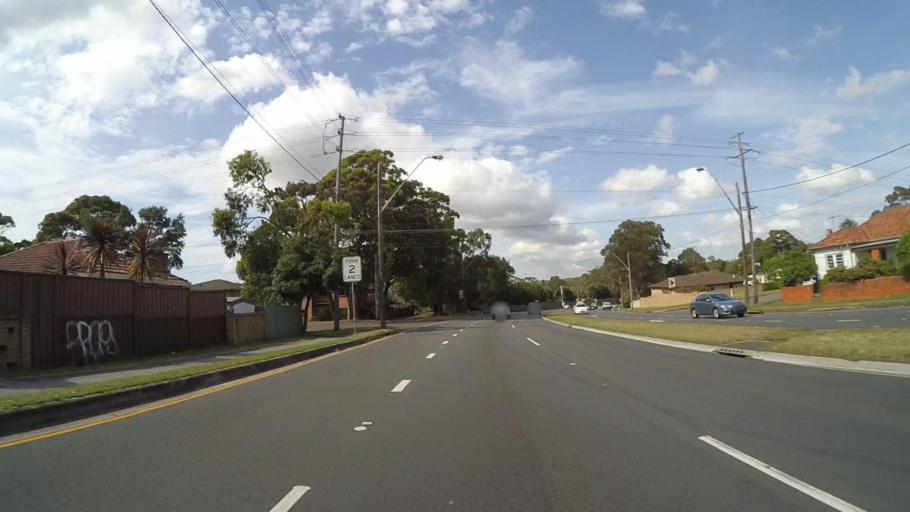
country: AU
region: New South Wales
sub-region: Sutherland Shire
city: Kirrawee
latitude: -34.0366
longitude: 151.0660
